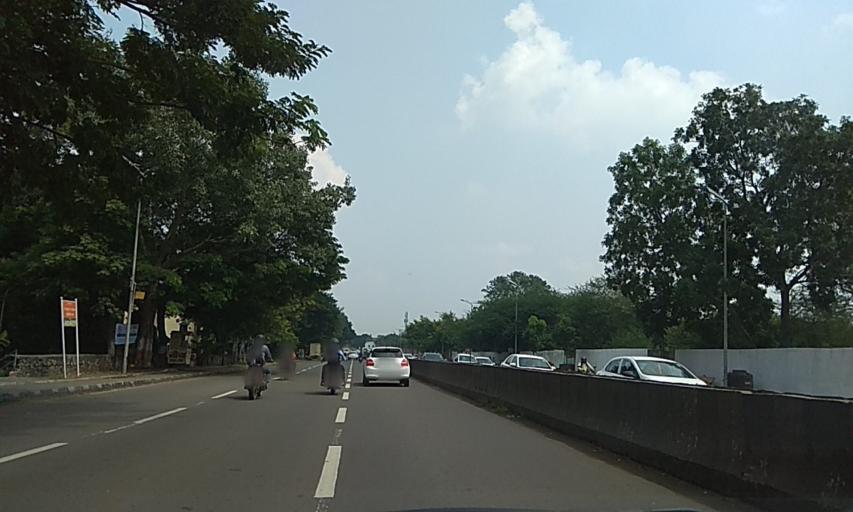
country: IN
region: Maharashtra
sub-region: Pune Division
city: Khadki
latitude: 18.5524
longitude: 73.8758
